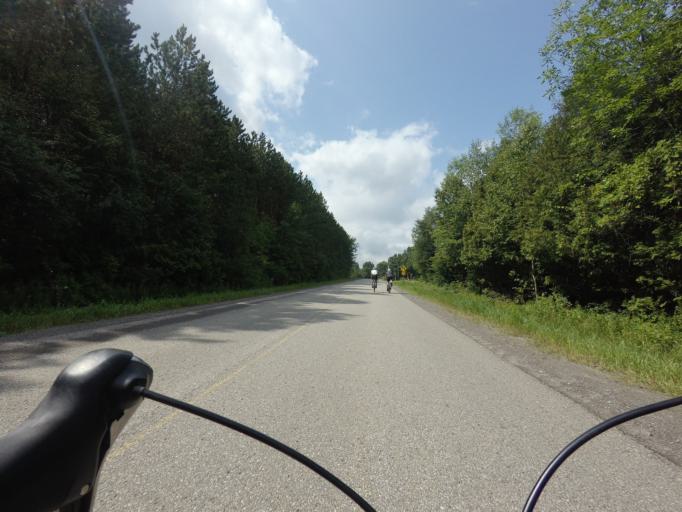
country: CA
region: Ontario
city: Brockville
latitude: 44.8031
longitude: -75.7206
